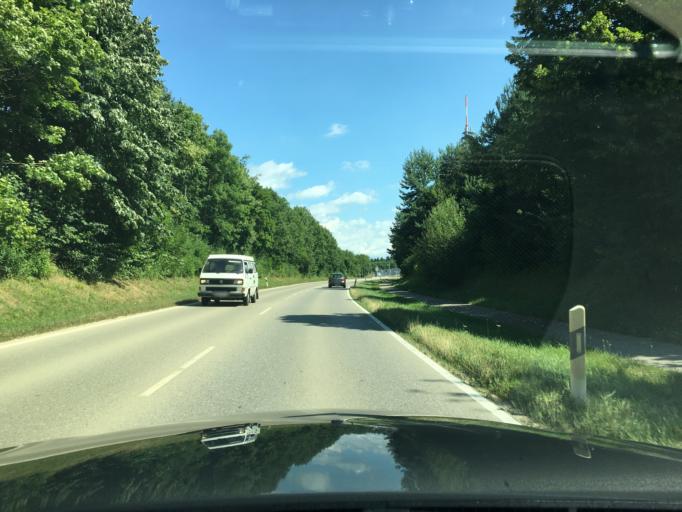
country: DE
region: Baden-Wuerttemberg
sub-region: Tuebingen Region
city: Dornstadt
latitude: 48.4223
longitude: 9.9346
